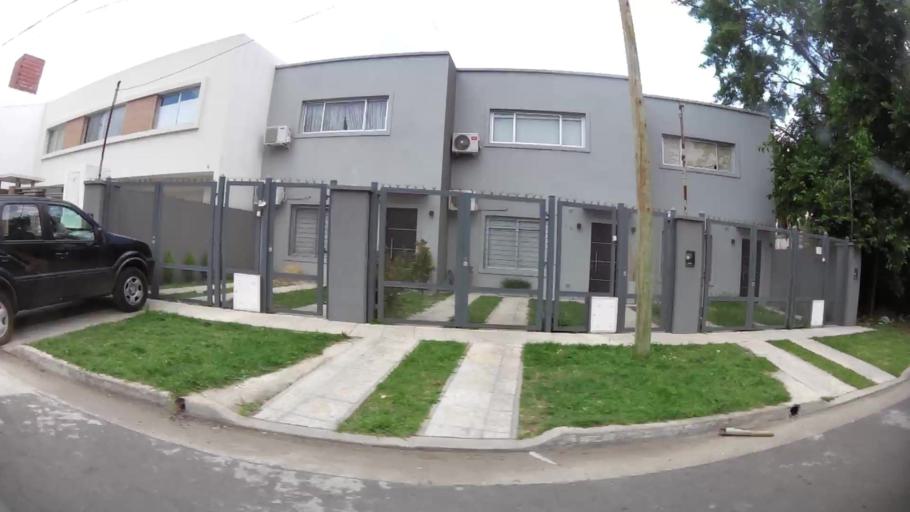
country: AR
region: Buenos Aires
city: Ituzaingo
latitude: -34.6390
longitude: -58.6752
